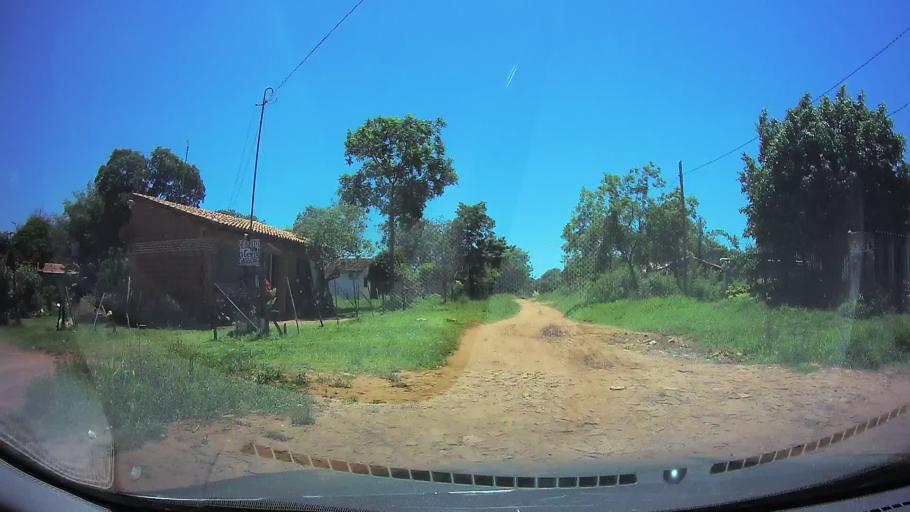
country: PY
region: Central
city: Limpio
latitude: -25.2417
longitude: -57.4861
